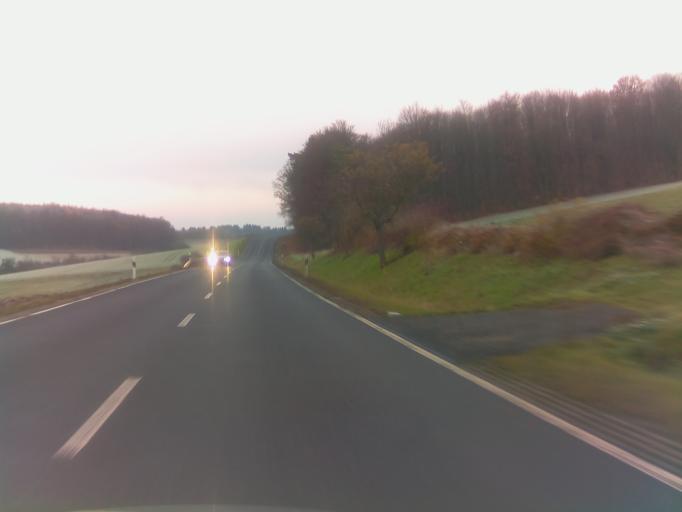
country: DE
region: Hesse
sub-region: Regierungsbezirk Kassel
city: Rasdorf
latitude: 50.7301
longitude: 9.9187
